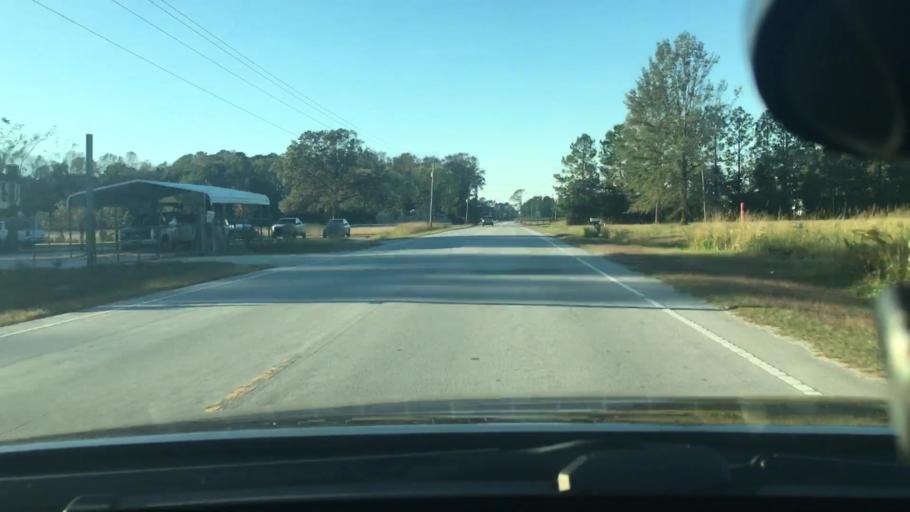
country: US
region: North Carolina
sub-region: Craven County
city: Vanceboro
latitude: 35.3489
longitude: -77.1858
